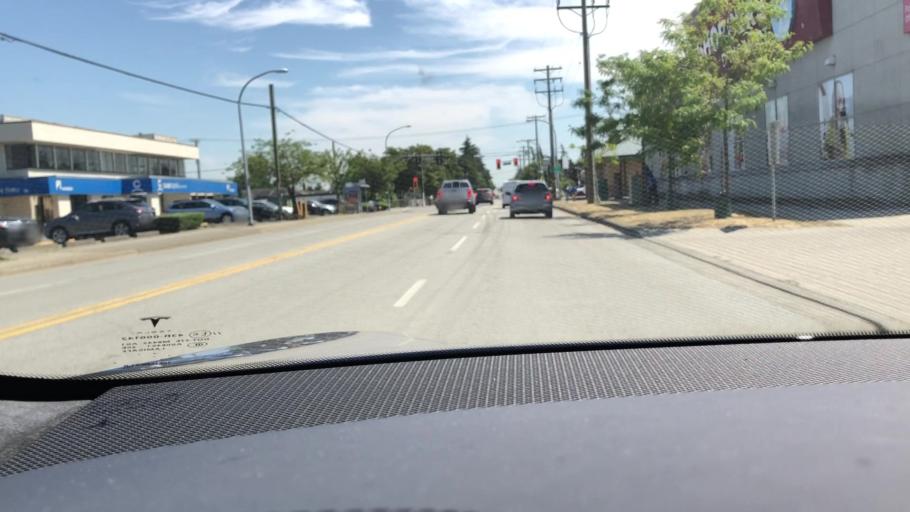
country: CA
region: British Columbia
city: Richmond
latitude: 49.1845
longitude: -123.0930
